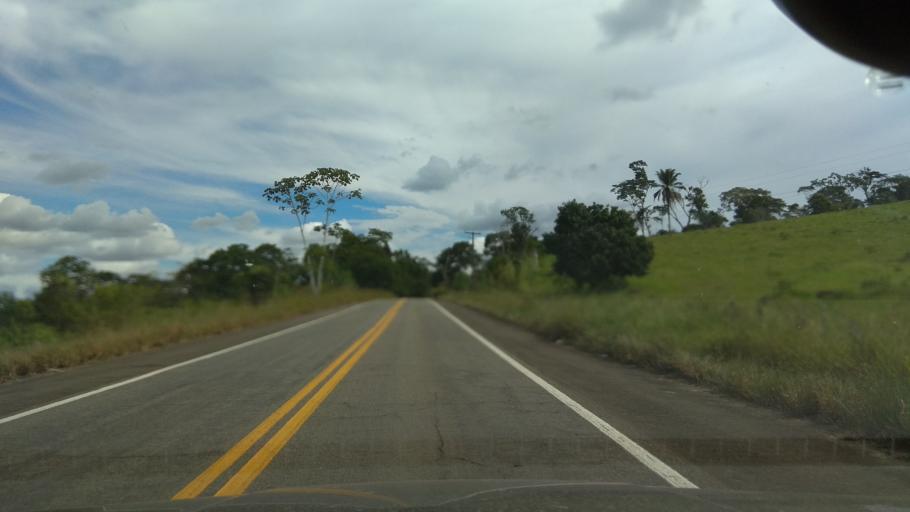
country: BR
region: Bahia
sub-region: Ubata
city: Ubata
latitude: -14.2257
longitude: -39.4700
